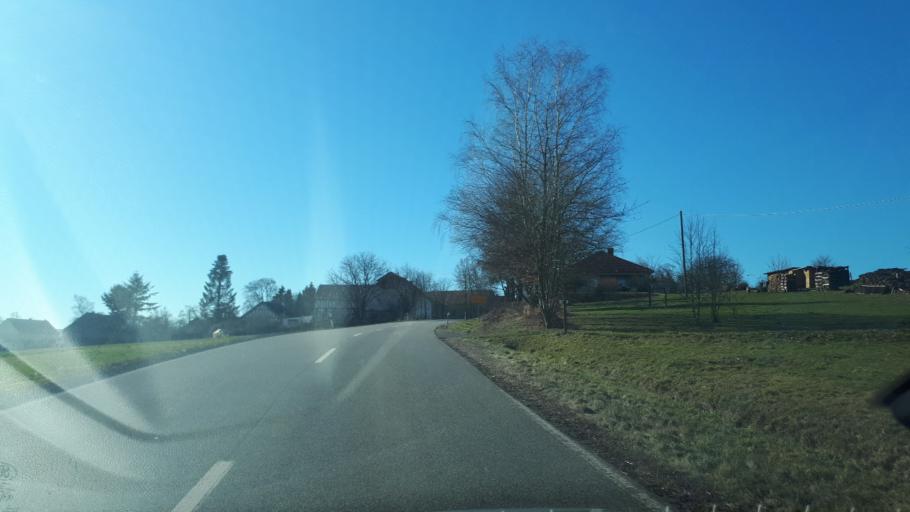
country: DE
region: Rheinland-Pfalz
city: Oberscheidweiler
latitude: 50.0763
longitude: 6.9372
